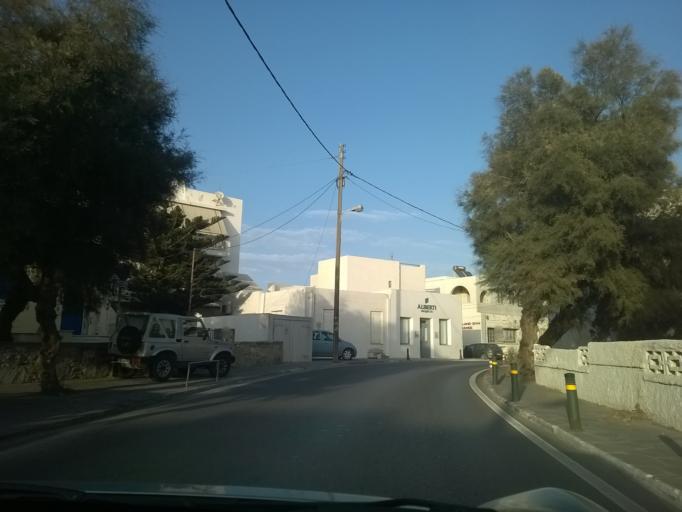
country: GR
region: South Aegean
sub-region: Nomos Kykladon
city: Naxos
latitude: 37.1080
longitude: 25.3762
